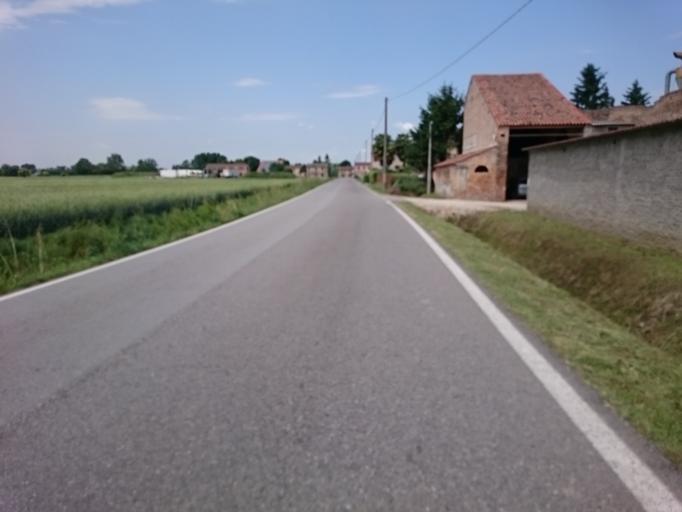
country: IT
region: Veneto
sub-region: Provincia di Padova
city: Carceri
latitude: 45.1896
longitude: 11.6282
